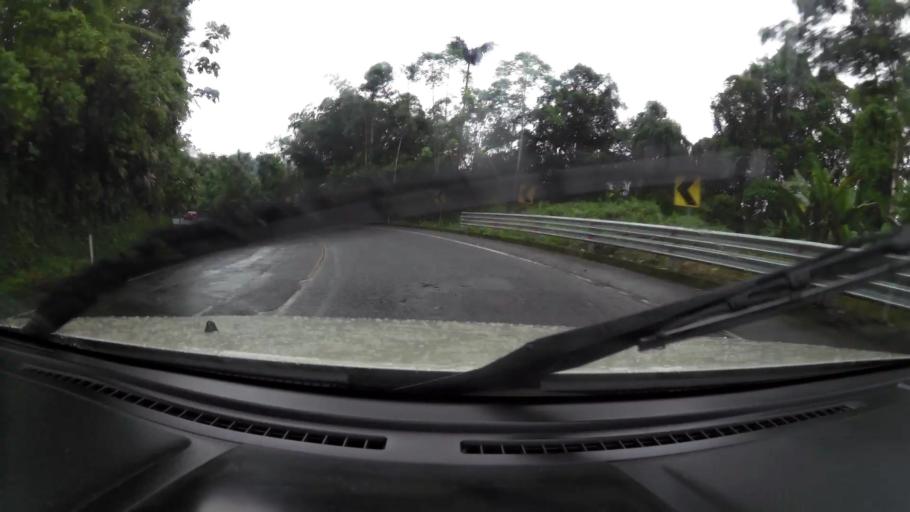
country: EC
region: Santo Domingo de los Tsachilas
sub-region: Canton Santo Domingo de los Colorados
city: Santo Domingo de los Colorados
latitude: -0.2341
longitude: -79.1372
